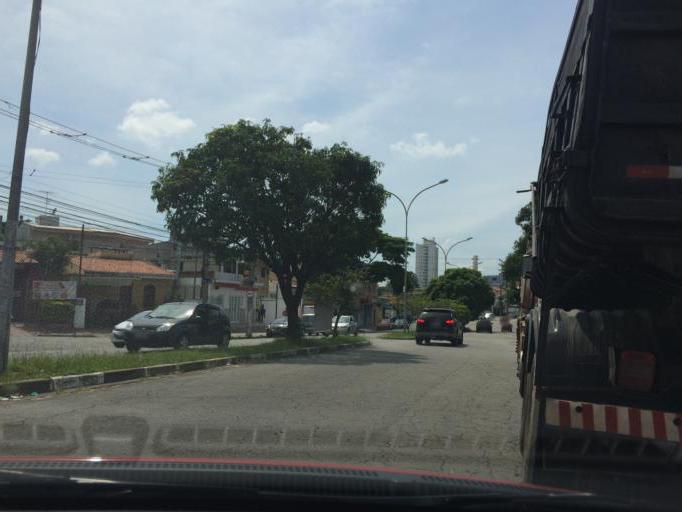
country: BR
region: Sao Paulo
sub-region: Osasco
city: Osasco
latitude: -23.5481
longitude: -46.7542
